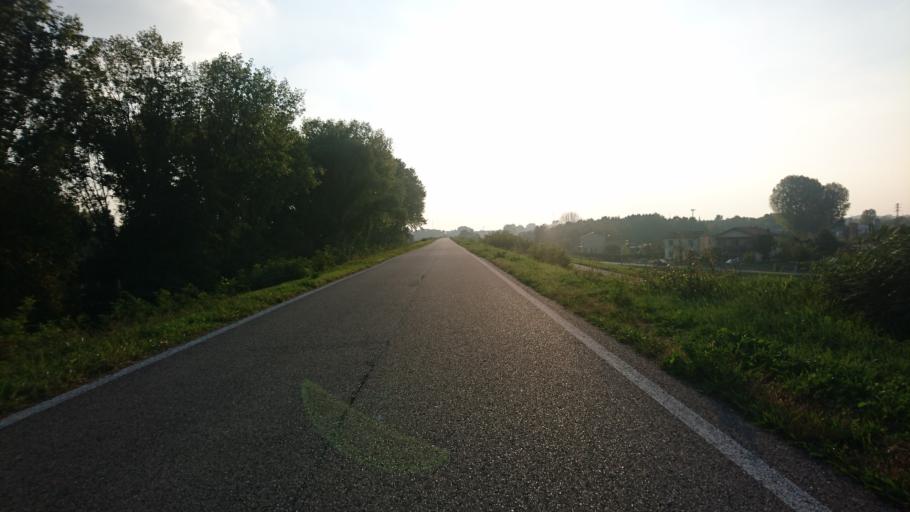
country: IT
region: Veneto
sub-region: Provincia di Rovigo
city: Santa Maria Maddalena
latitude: 44.8942
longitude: 11.6276
